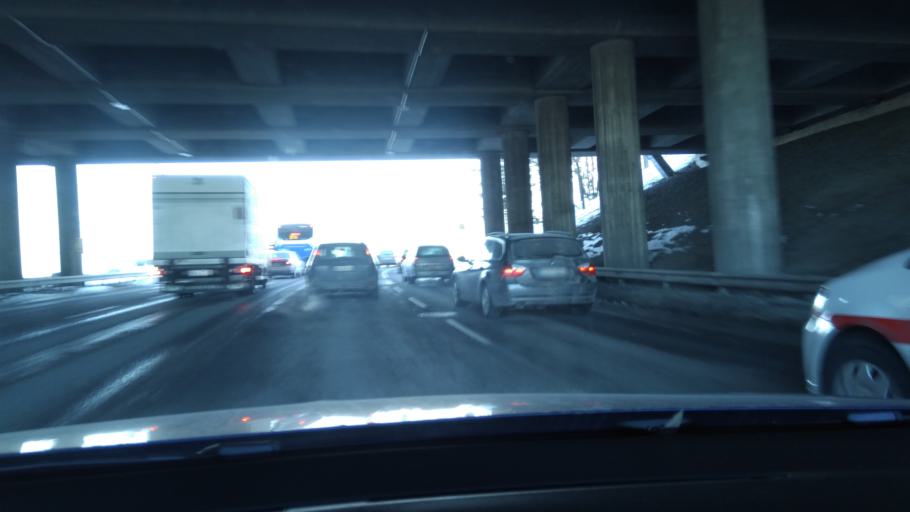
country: FI
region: Pirkanmaa
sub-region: Tampere
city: Pirkkala
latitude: 61.5092
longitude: 23.6886
